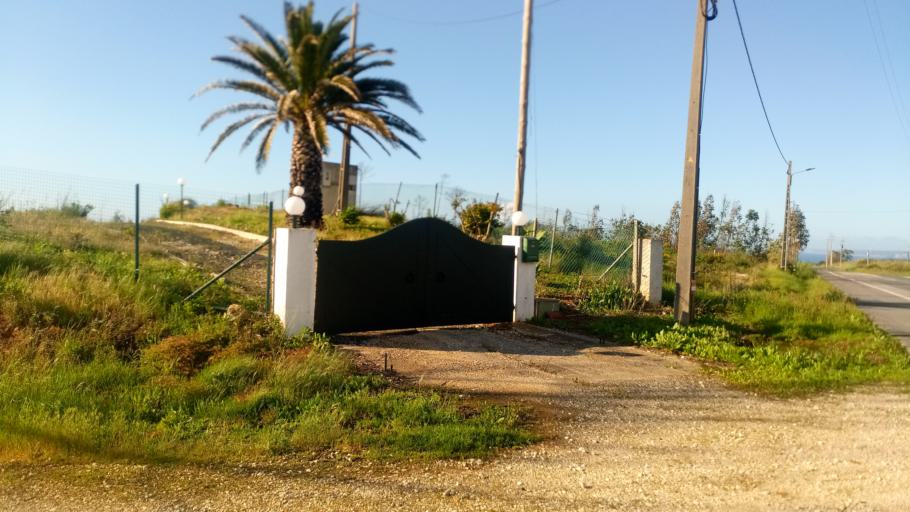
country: PT
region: Leiria
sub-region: Caldas da Rainha
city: Caldas da Rainha
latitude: 39.4624
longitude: -9.1974
